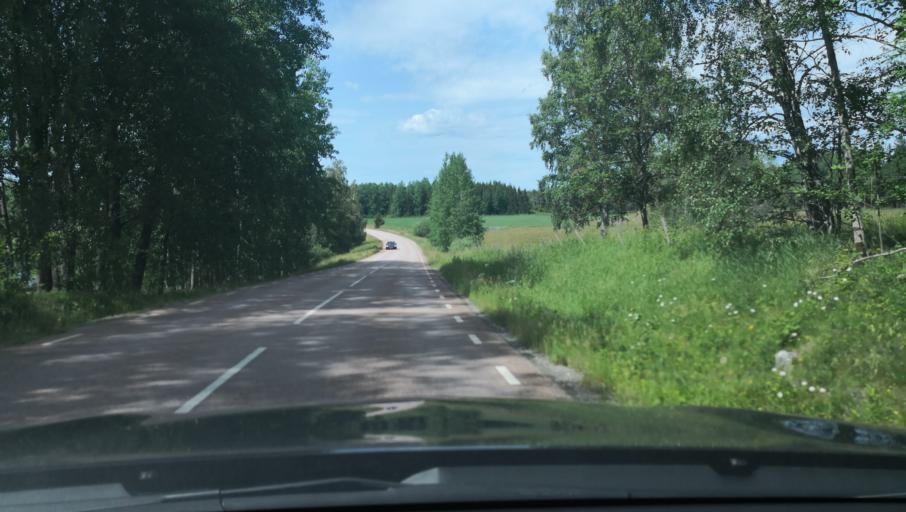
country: SE
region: Vaestmanland
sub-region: Surahammars Kommun
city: Ramnas
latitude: 59.8282
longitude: 16.1418
